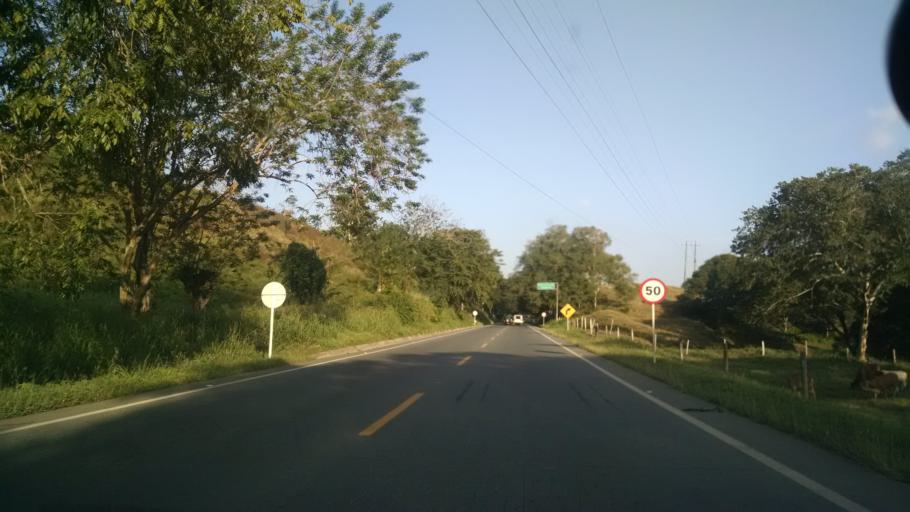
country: CO
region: Cordoba
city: Canalete
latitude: 8.8469
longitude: -76.1418
